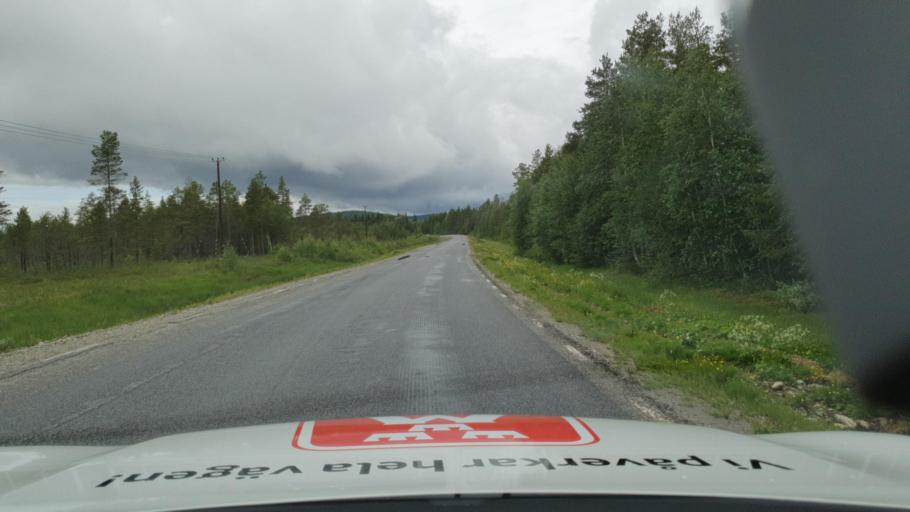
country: SE
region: Vaesterbotten
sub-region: Dorotea Kommun
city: Dorotea
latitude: 64.1821
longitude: 16.6265
